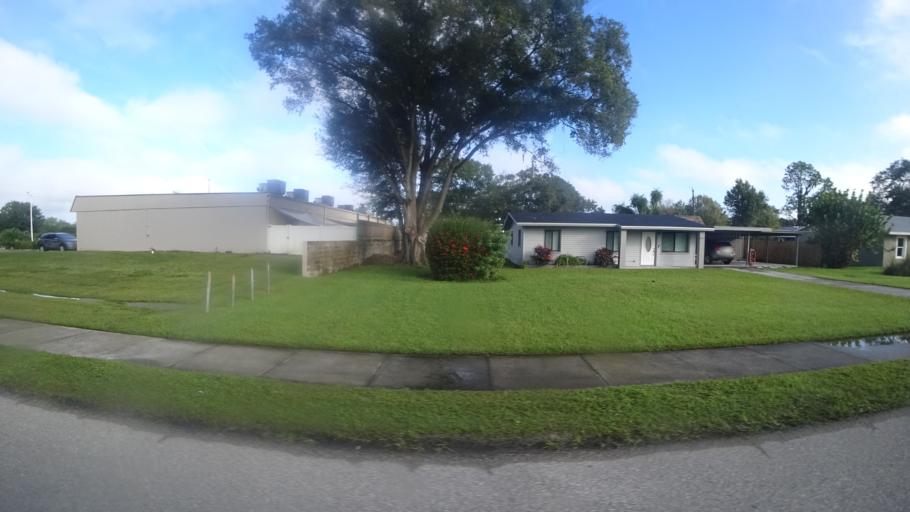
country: US
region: Florida
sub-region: Manatee County
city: Ellenton
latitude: 27.5392
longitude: -82.4821
